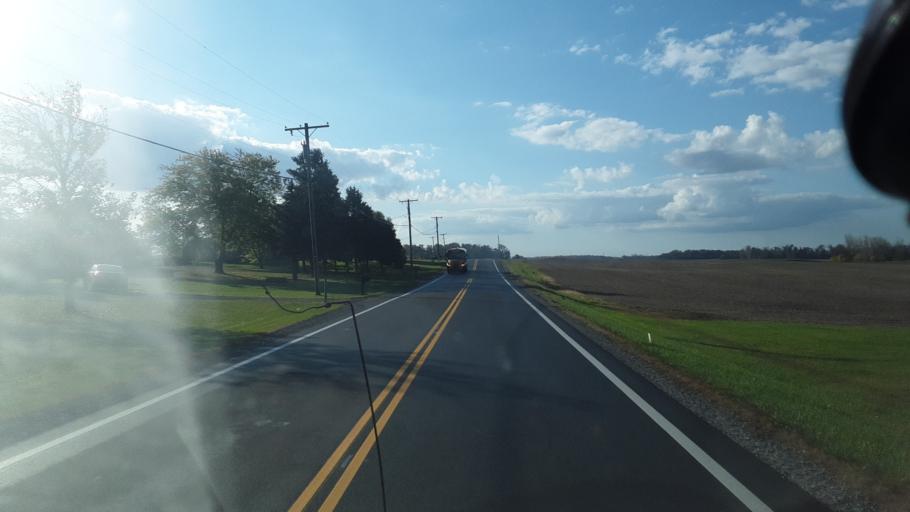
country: US
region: Ohio
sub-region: Fayette County
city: Jeffersonville
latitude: 39.6135
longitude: -83.5262
